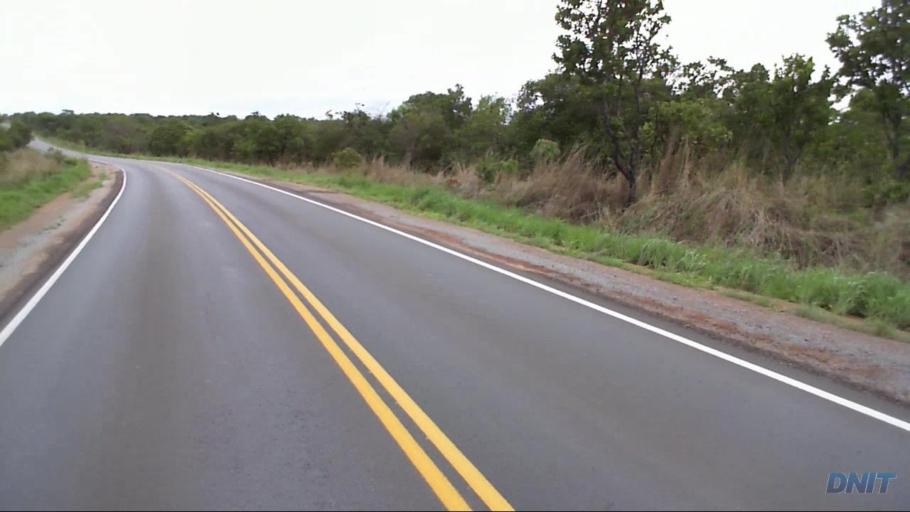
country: BR
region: Goias
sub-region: Padre Bernardo
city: Padre Bernardo
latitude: -15.4000
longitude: -48.1999
